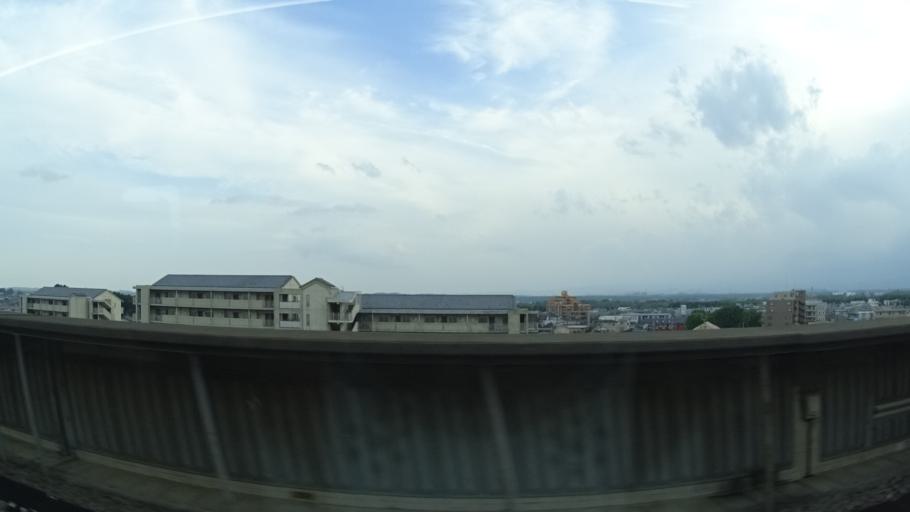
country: JP
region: Saitama
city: Kumagaya
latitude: 36.1372
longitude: 139.3954
